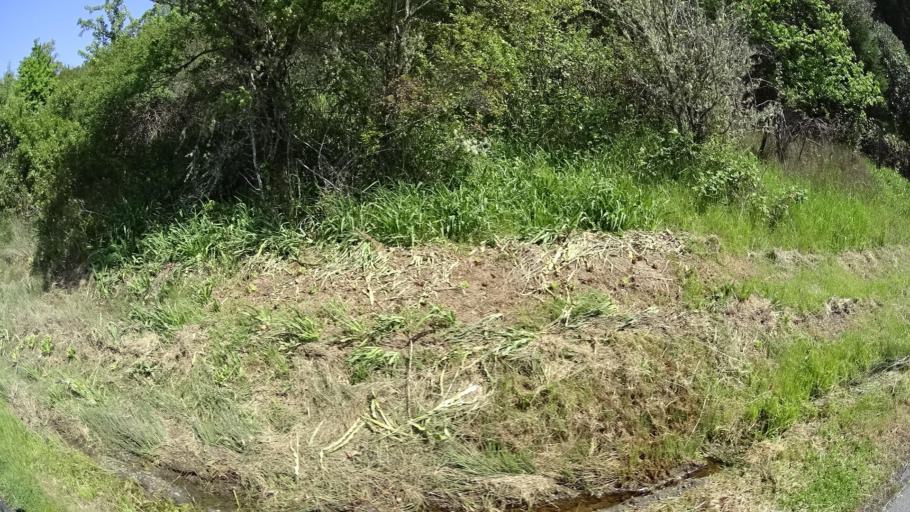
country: US
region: California
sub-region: Humboldt County
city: Redway
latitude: 40.2661
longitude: -123.6276
